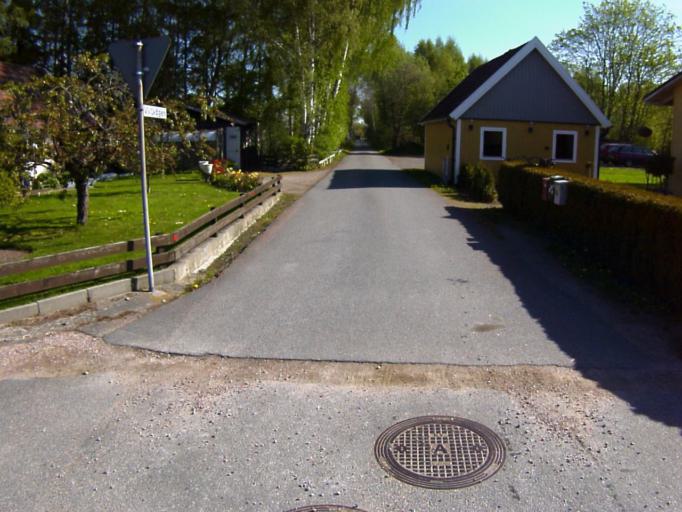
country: SE
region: Skane
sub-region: Kristianstads Kommun
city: Onnestad
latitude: 55.9341
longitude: 13.9602
